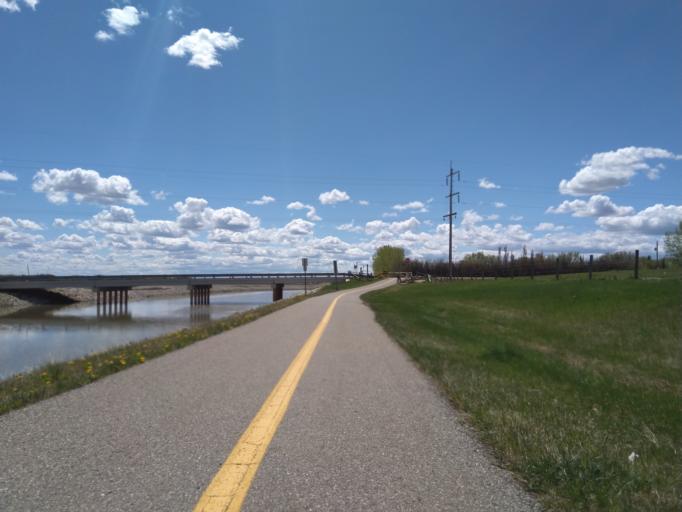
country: CA
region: Alberta
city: Chestermere
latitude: 51.0095
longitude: -113.8471
